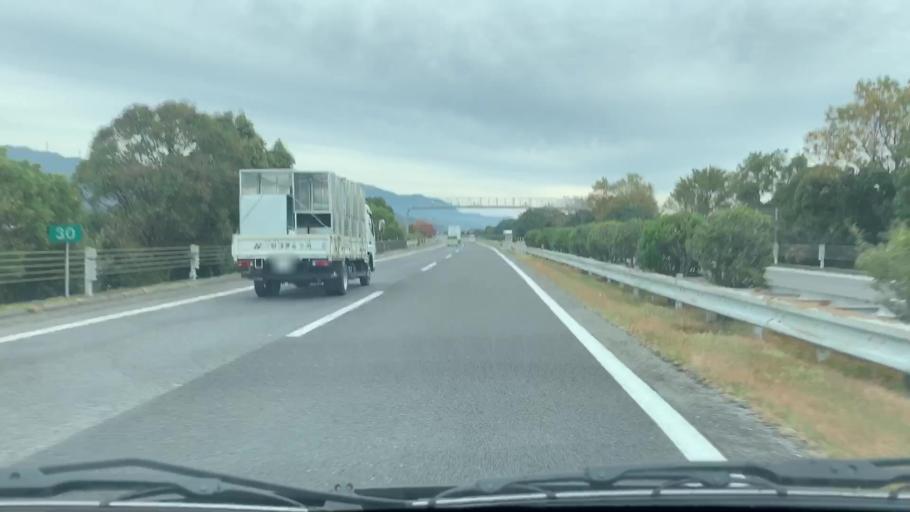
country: JP
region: Saga Prefecture
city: Saga-shi
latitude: 33.3092
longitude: 130.2451
